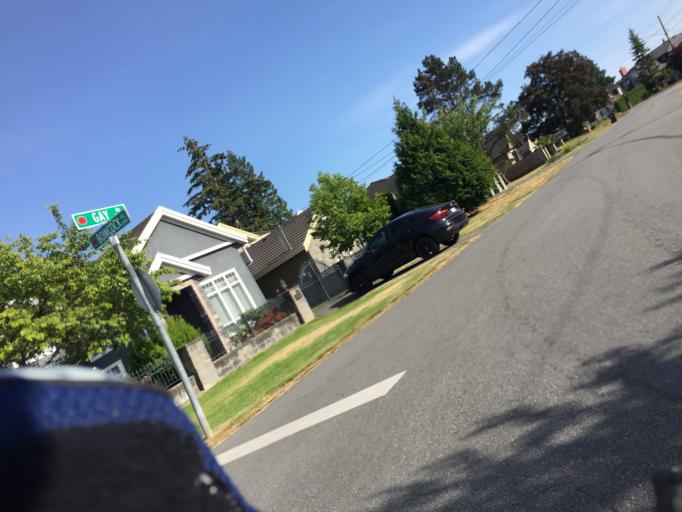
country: CA
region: British Columbia
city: Richmond
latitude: 49.1507
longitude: -123.1352
